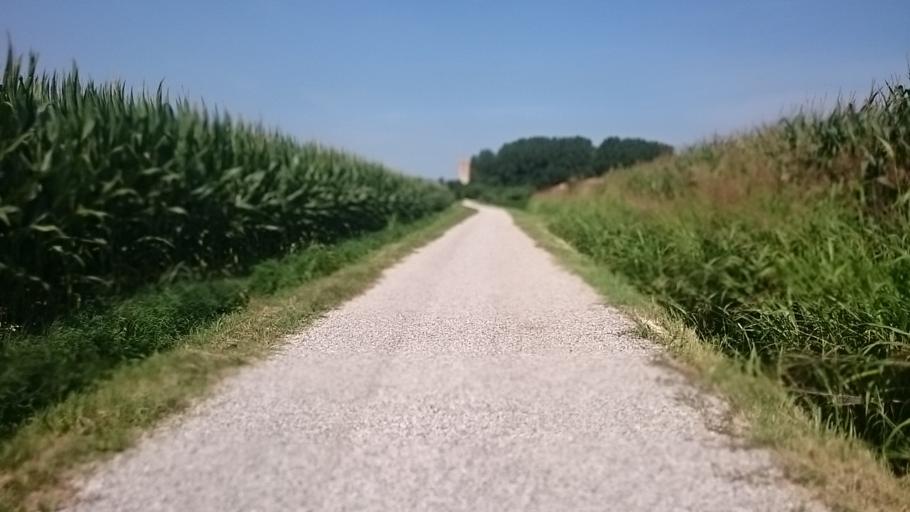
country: IT
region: Veneto
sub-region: Provincia di Padova
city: Cervarese Santa Croce
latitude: 45.4133
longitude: 11.7169
